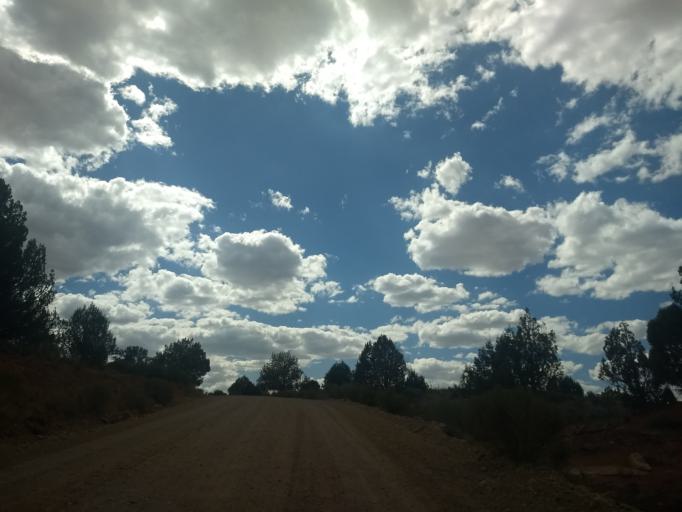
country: US
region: Utah
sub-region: Kane County
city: Kanab
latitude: 37.1520
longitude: -112.5430
